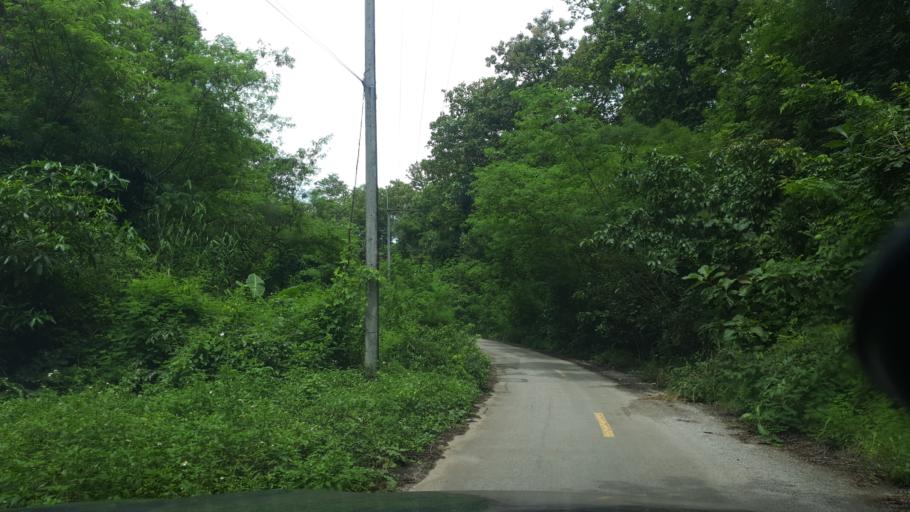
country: TH
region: Lampang
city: Hang Chat
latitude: 18.3510
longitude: 99.2529
